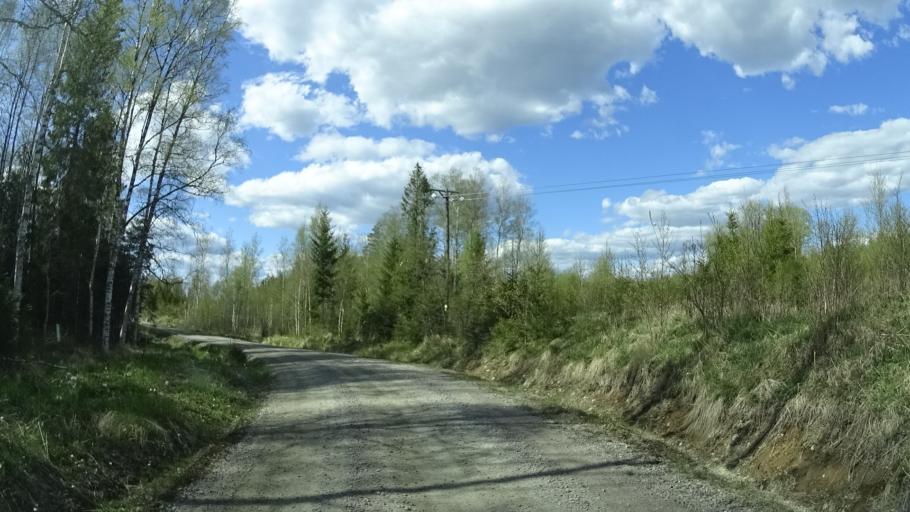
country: SE
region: OErebro
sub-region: Orebro Kommun
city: Garphyttan
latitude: 59.4161
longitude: 14.8739
